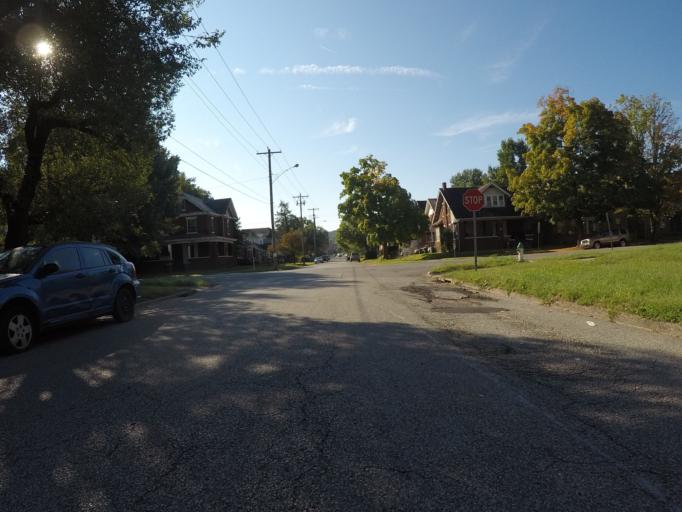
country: US
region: West Virginia
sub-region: Cabell County
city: Huntington
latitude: 38.4148
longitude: -82.4368
